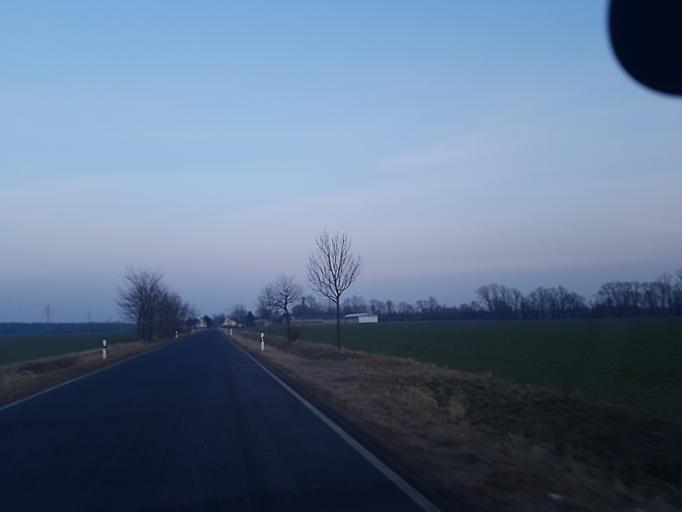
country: DE
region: Saxony-Anhalt
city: Holzdorf
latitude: 51.7655
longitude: 13.0959
